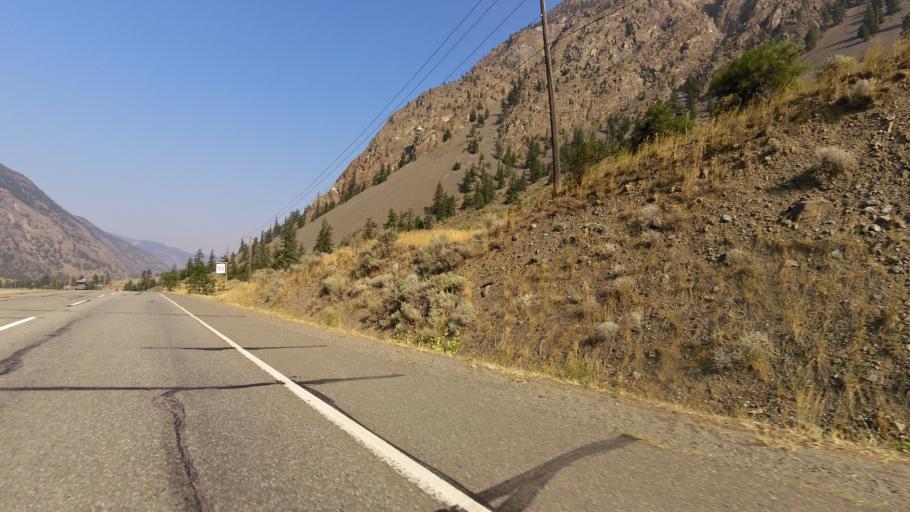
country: CA
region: British Columbia
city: Oliver
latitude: 49.2049
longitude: -119.8676
